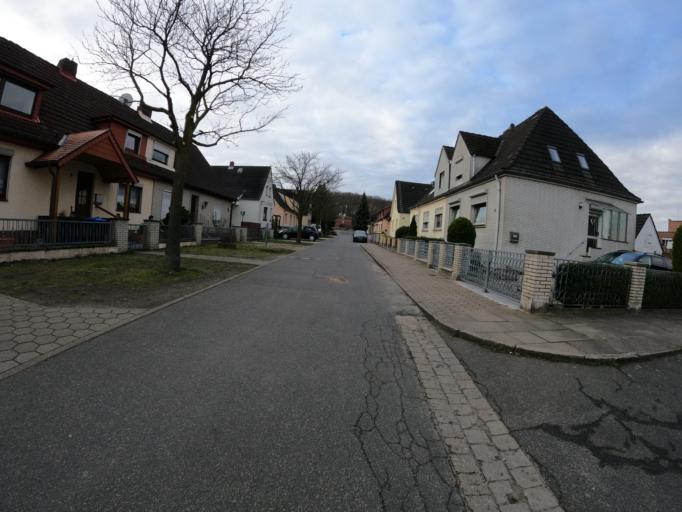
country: DE
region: Hamburg
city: Harburg
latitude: 53.4729
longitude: 9.9266
